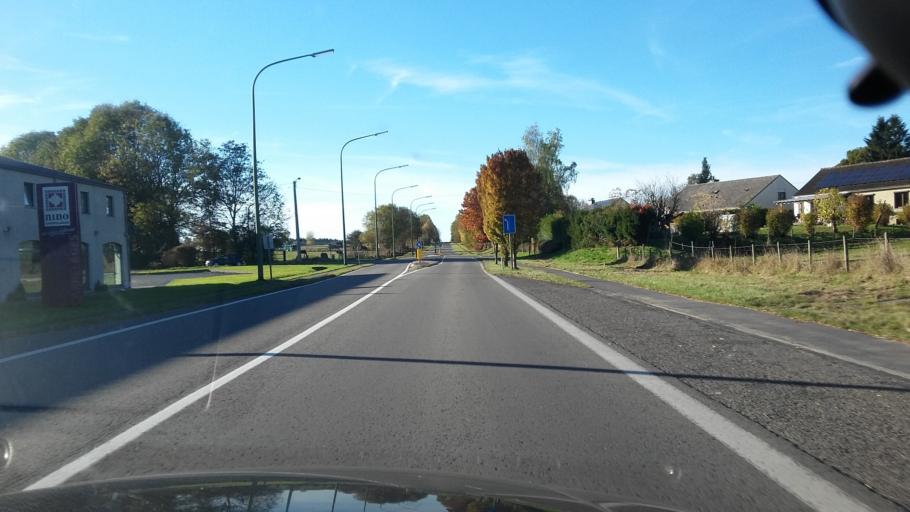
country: BE
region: Wallonia
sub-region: Province du Luxembourg
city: Saint-Leger
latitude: 49.6687
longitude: 5.6638
